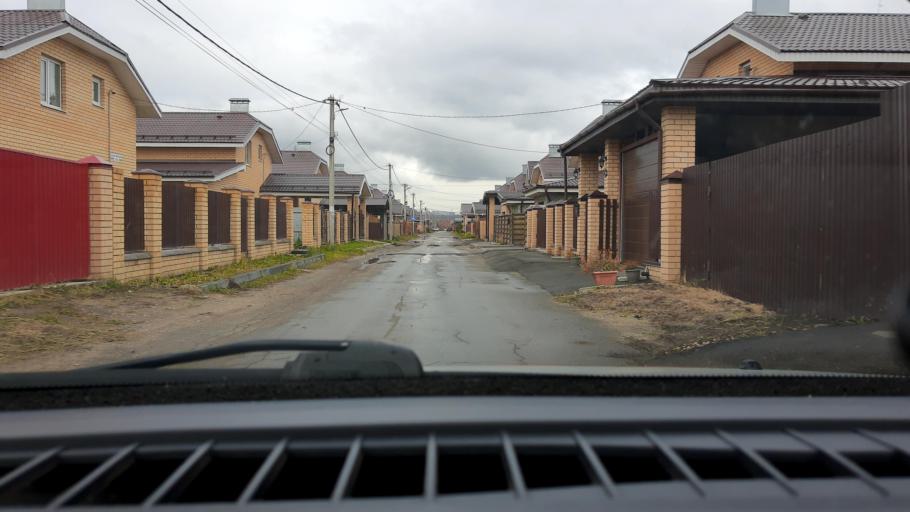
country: RU
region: Nizjnij Novgorod
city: Afonino
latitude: 56.2014
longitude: 44.1291
